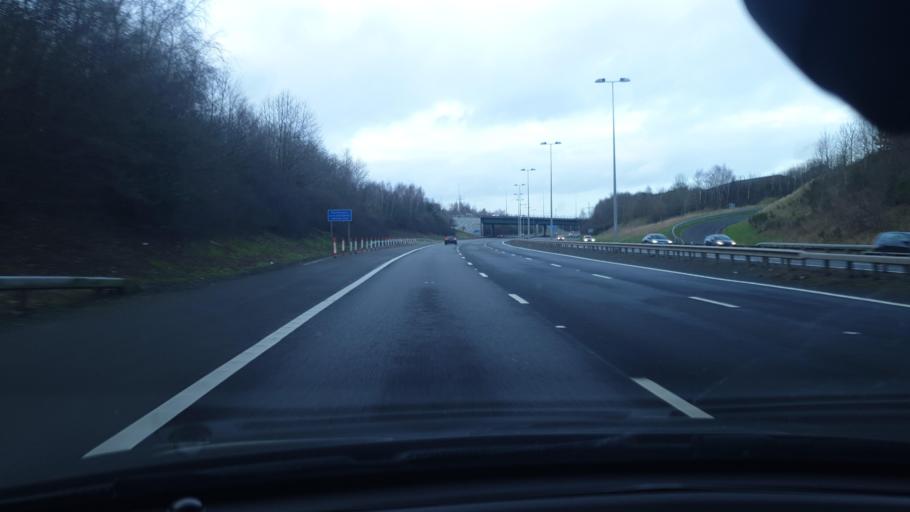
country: GB
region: England
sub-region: Solihull
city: Chelmsley Wood
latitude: 52.4819
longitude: -1.7072
